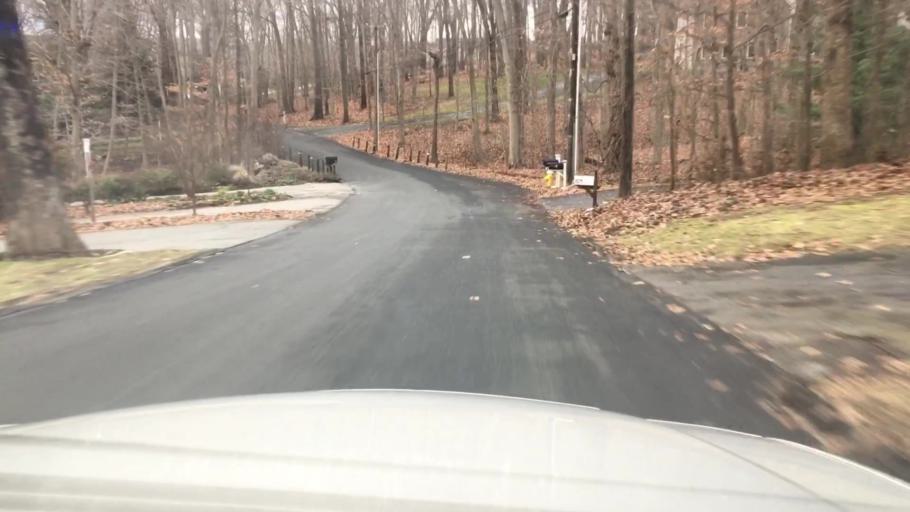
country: US
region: Connecticut
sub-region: Middlesex County
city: Essex Village
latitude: 41.3581
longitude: -72.3996
